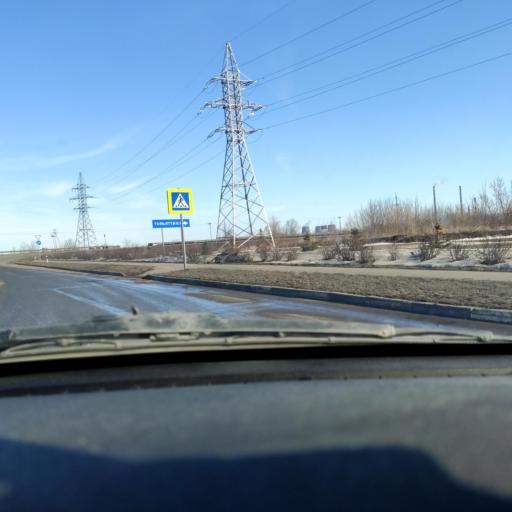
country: RU
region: Samara
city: Podstepki
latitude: 53.5593
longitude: 49.2043
